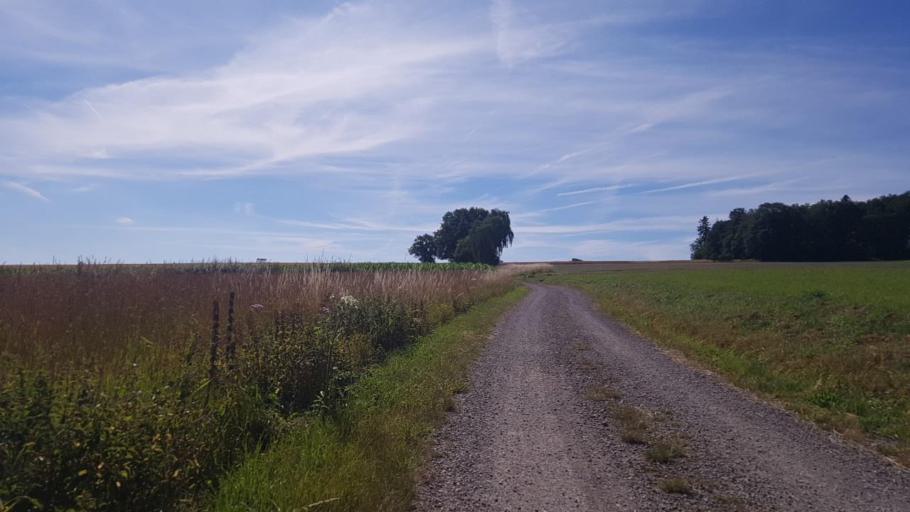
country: DE
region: North Rhine-Westphalia
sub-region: Regierungsbezirk Koln
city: Kall
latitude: 50.6192
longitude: 6.5547
